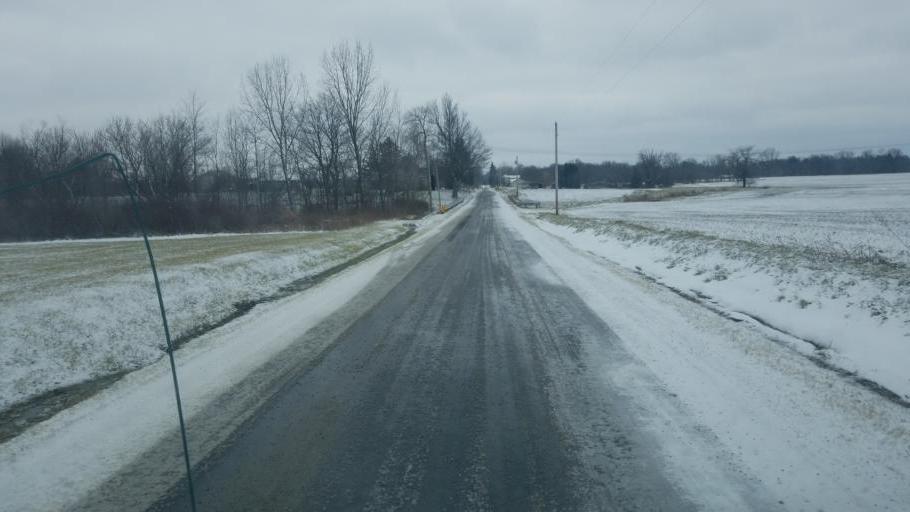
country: US
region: Ohio
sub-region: Delaware County
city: Sunbury
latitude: 40.2182
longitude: -82.7699
